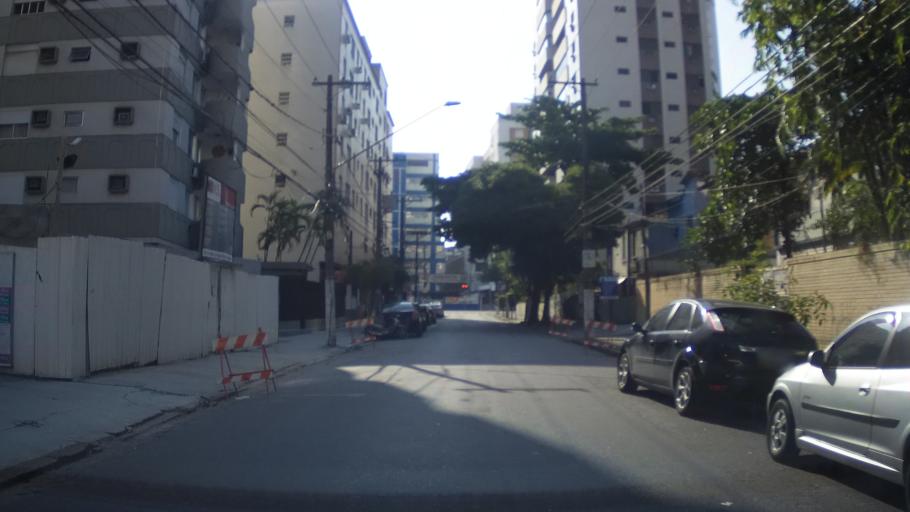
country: BR
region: Sao Paulo
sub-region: Santos
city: Santos
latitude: -23.9629
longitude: -46.3245
